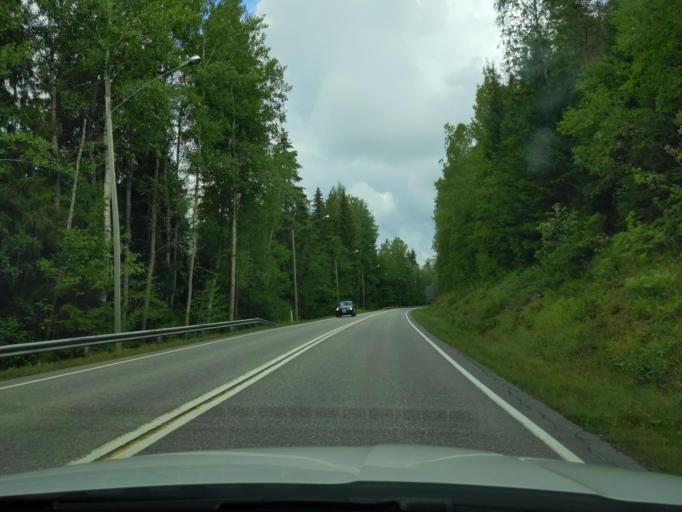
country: FI
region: Uusimaa
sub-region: Porvoo
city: Porvoo
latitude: 60.4492
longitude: 25.7296
